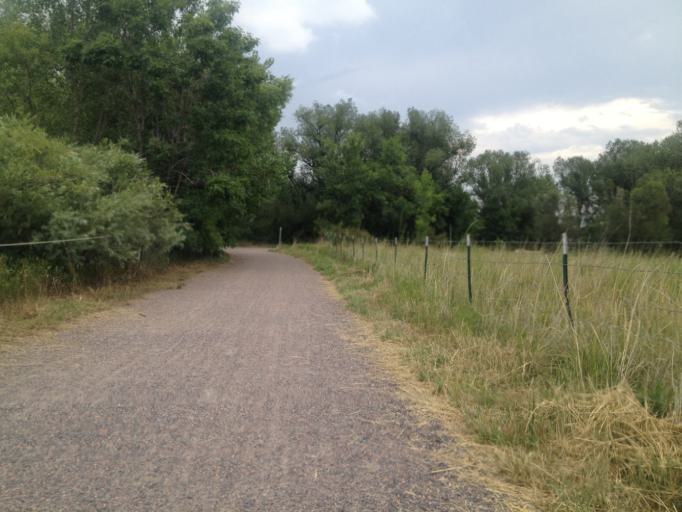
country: US
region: Colorado
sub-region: Boulder County
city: Louisville
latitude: 39.9625
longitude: -105.1422
